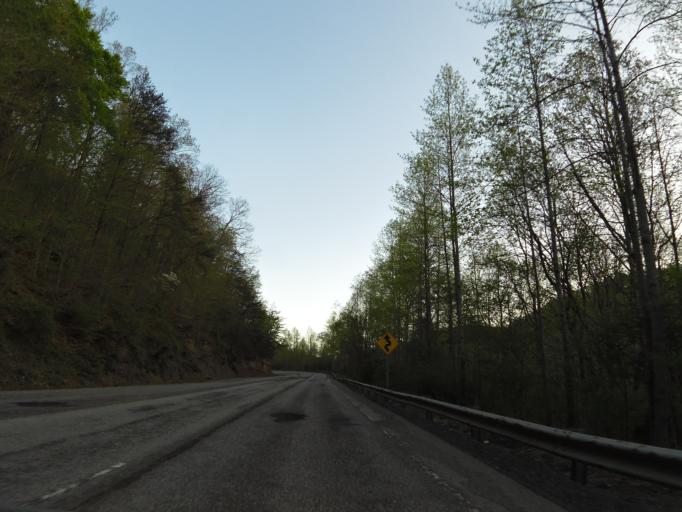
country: US
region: Tennessee
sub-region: Campbell County
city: Fincastle
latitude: 36.4612
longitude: -84.0798
